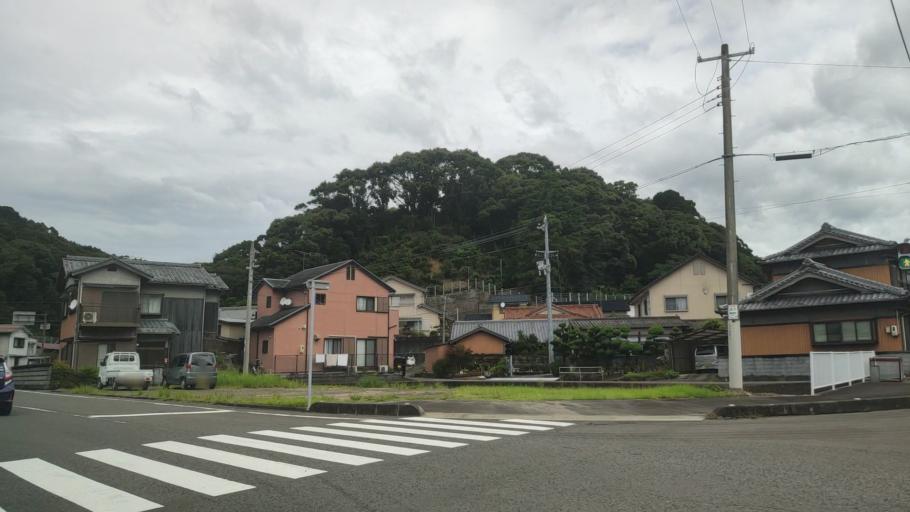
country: JP
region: Wakayama
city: Tanabe
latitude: 33.6805
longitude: 135.3889
